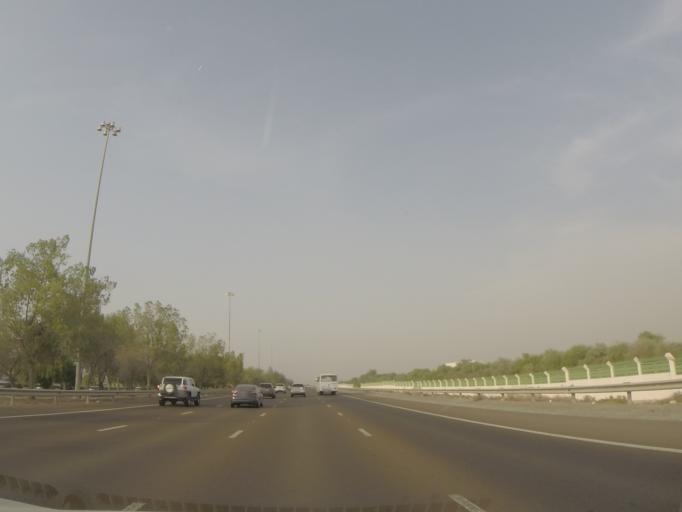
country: AE
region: Abu Dhabi
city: Abu Dhabi
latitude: 24.7131
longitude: 54.7984
